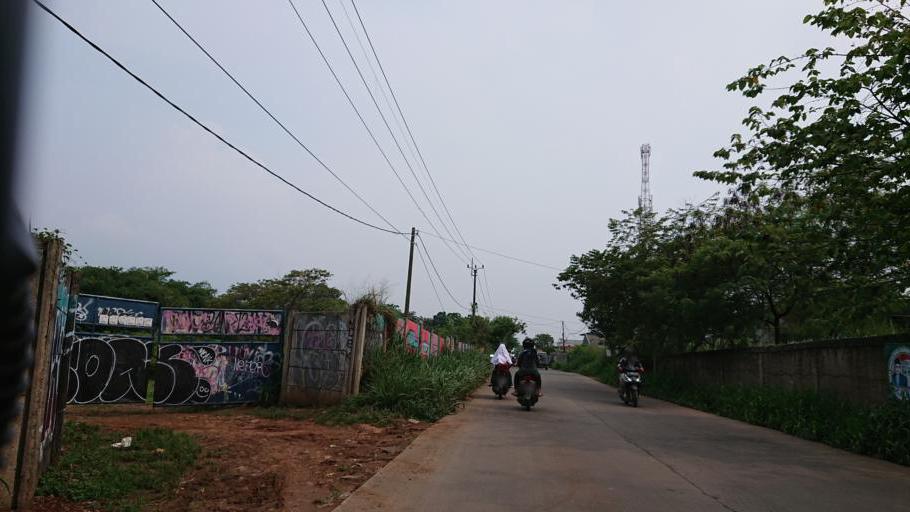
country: ID
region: West Java
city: Parung
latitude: -6.4045
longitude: 106.6924
